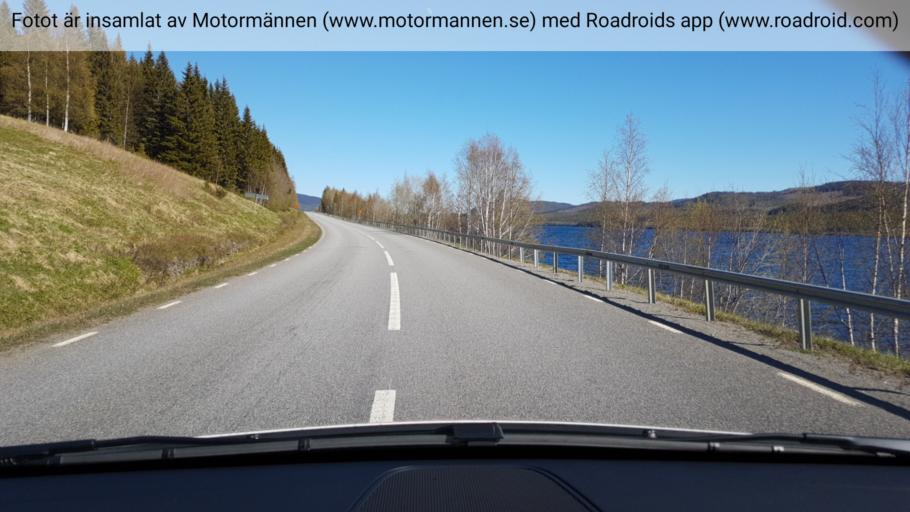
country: NO
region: Nord-Trondelag
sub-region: Lierne
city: Sandvika
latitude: 64.3851
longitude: 14.5348
